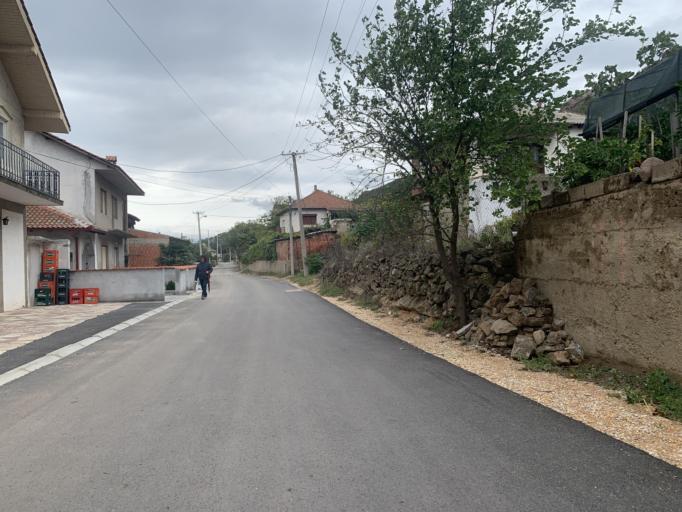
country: MK
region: Bogdanci
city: Bogdanci
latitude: 41.1909
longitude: 22.5393
